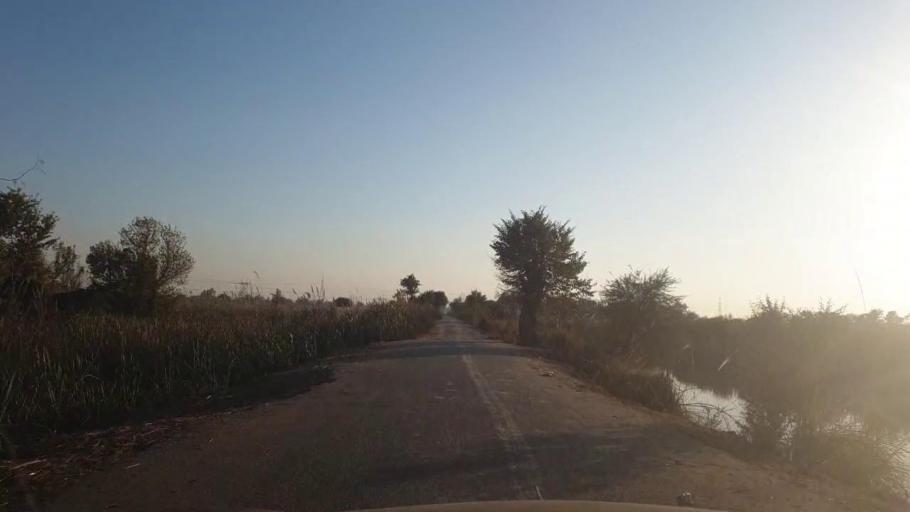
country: PK
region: Sindh
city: Mirpur Mathelo
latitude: 27.9971
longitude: 69.4671
